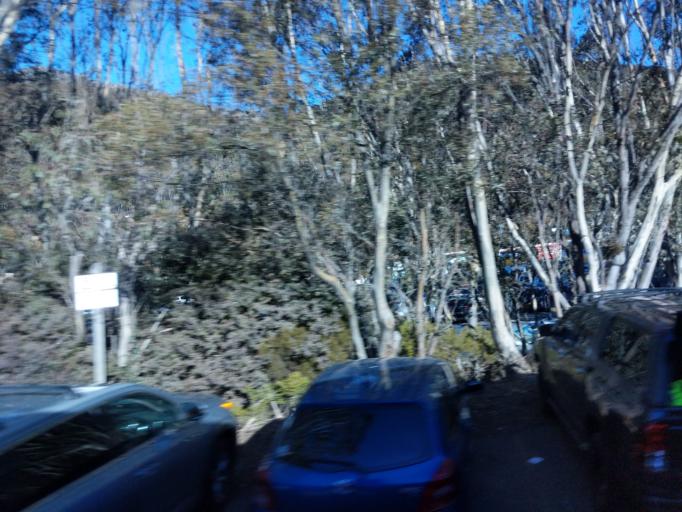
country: AU
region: New South Wales
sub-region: Snowy River
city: Jindabyne
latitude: -36.4984
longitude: 148.3130
